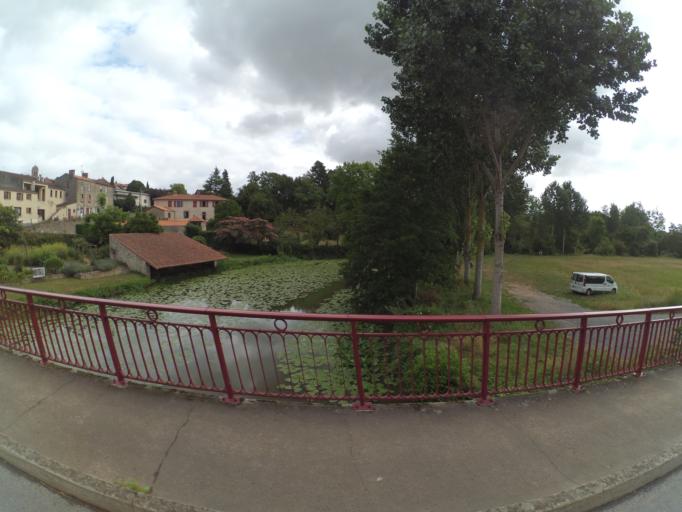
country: FR
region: Pays de la Loire
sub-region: Departement de Maine-et-Loire
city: Montfaucon-Montigne
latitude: 47.0982
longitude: -1.1268
